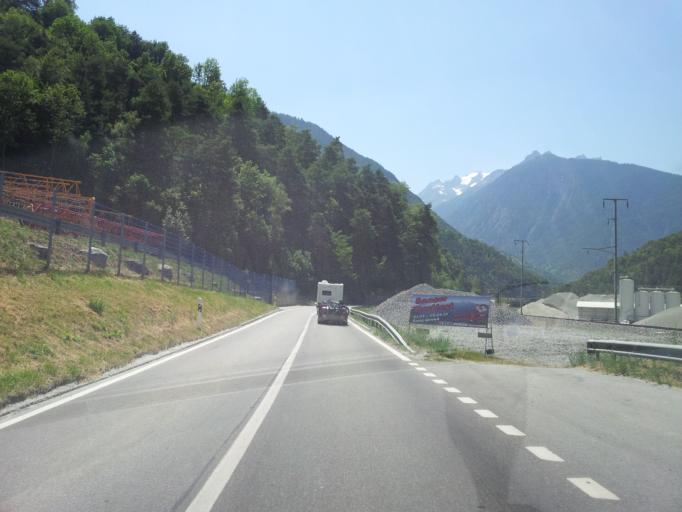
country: CH
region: Valais
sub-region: Visp District
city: Visperterminen
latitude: 46.2648
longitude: 7.8794
